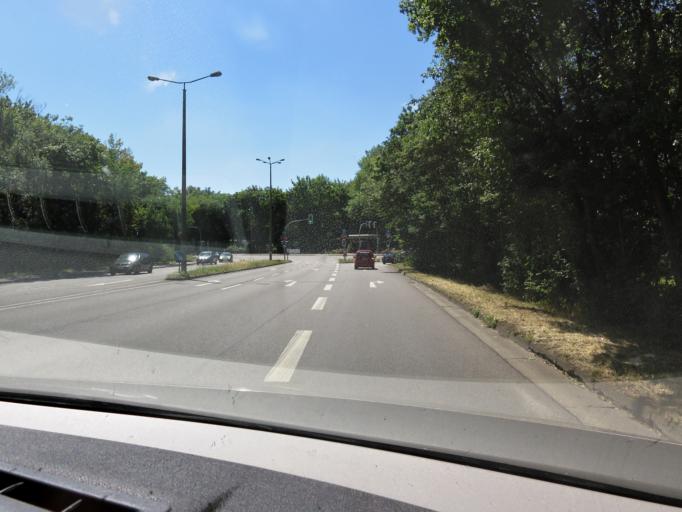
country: DE
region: Saxony-Anhalt
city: Merseburg
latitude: 51.3469
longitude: 11.9864
